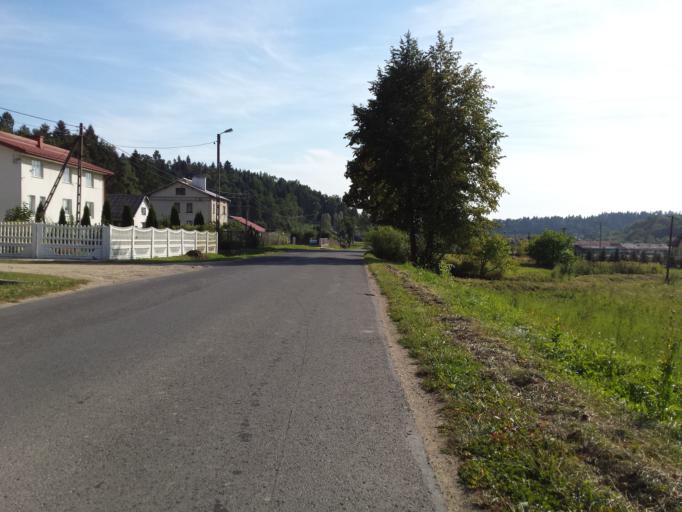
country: PL
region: Subcarpathian Voivodeship
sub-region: Powiat leski
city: Olszanica
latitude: 49.4934
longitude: 22.4496
